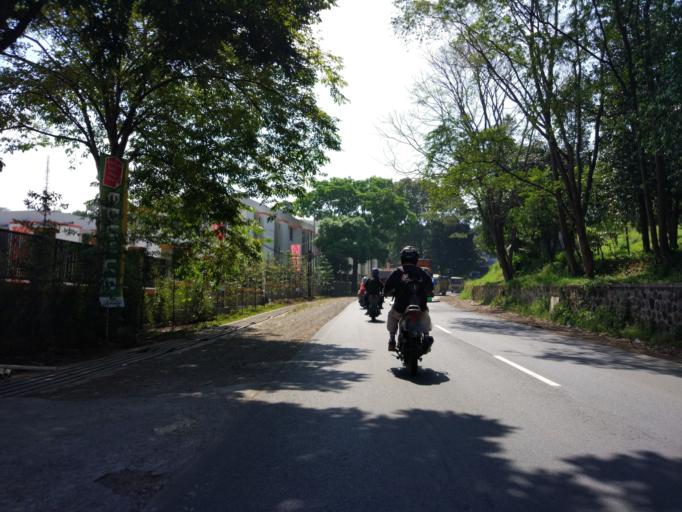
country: ID
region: West Java
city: Cileunyi
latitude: -6.9275
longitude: 107.7844
